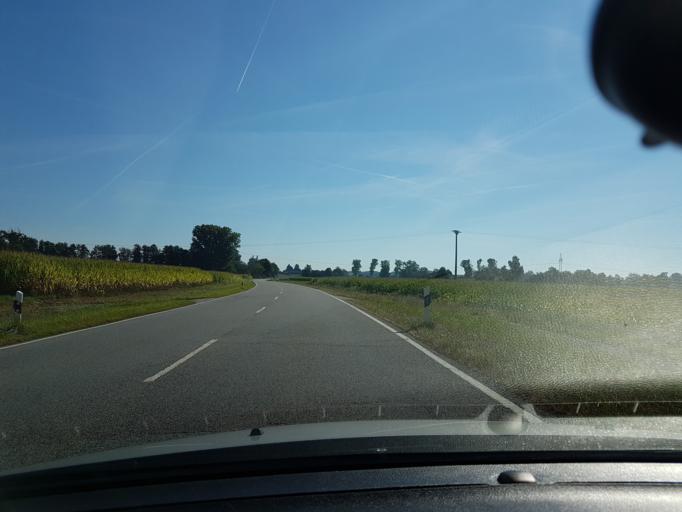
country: DE
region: Bavaria
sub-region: Upper Bavaria
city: Aham
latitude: 48.3504
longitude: 12.2046
